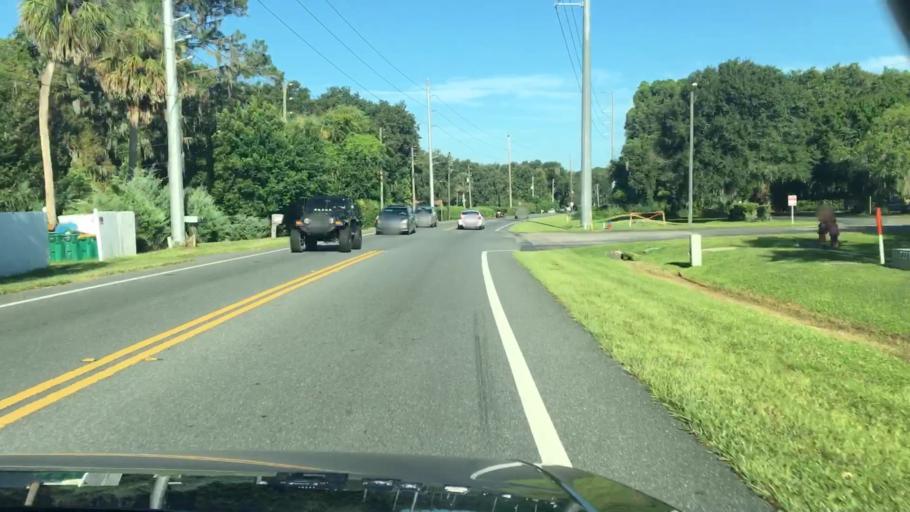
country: US
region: Florida
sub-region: Lake County
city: Eustis
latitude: 28.8741
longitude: -81.7035
